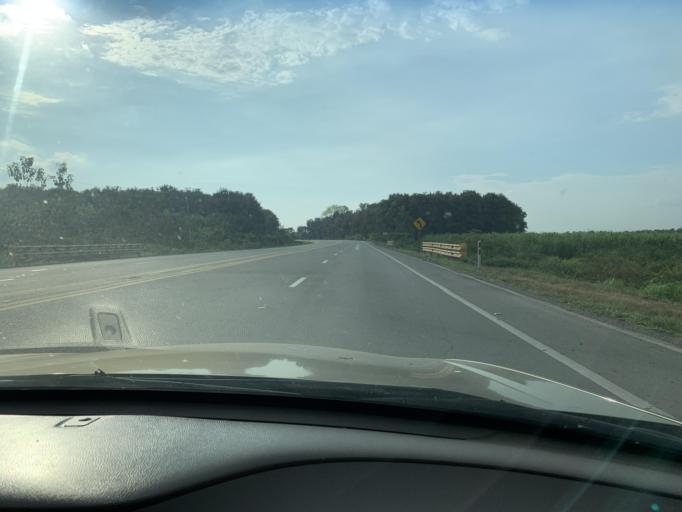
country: EC
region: Guayas
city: Coronel Marcelino Mariduena
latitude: -2.2820
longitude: -79.5181
